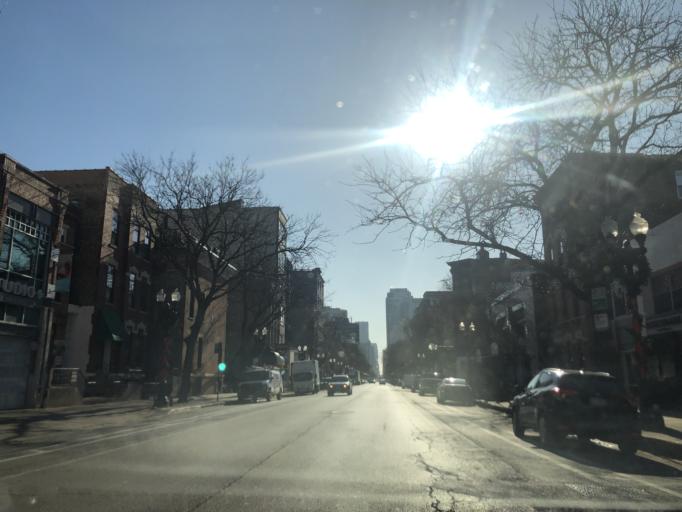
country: US
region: Illinois
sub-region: Cook County
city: Chicago
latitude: 41.9099
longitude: -87.6347
